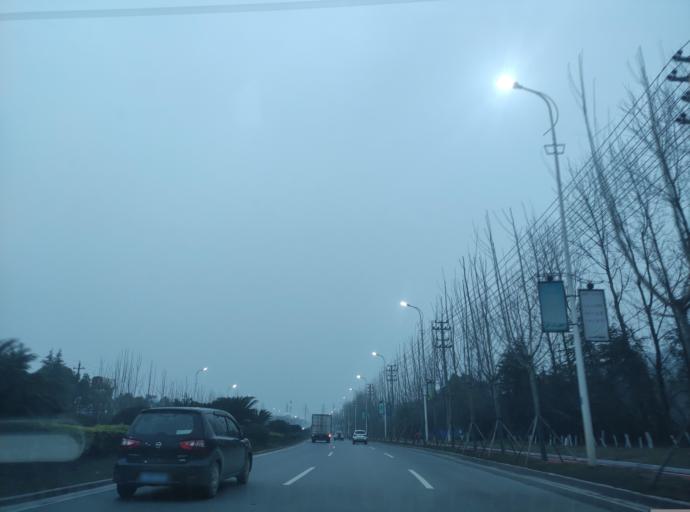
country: CN
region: Jiangxi Sheng
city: Pingxiang
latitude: 27.6654
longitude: 113.8756
